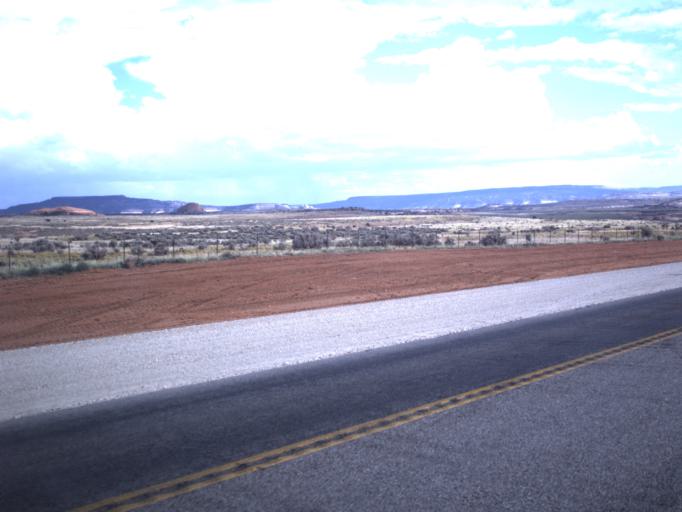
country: US
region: Utah
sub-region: San Juan County
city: Monticello
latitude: 38.2111
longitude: -109.3736
